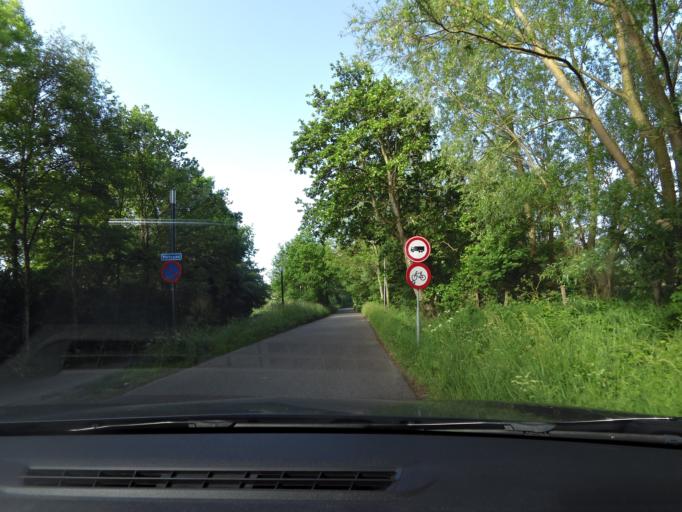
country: NL
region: Zeeland
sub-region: Schouwen-Duiveland
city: Renesse
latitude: 51.7392
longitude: 3.7835
